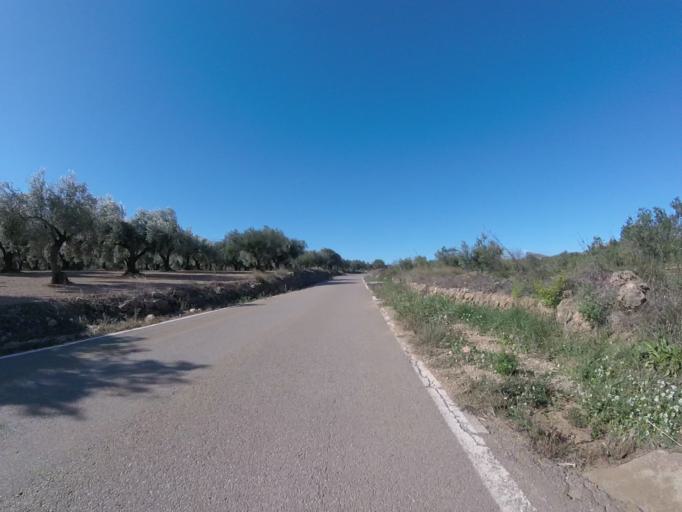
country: ES
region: Valencia
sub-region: Provincia de Castello
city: Chert/Xert
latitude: 40.4541
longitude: 0.1325
